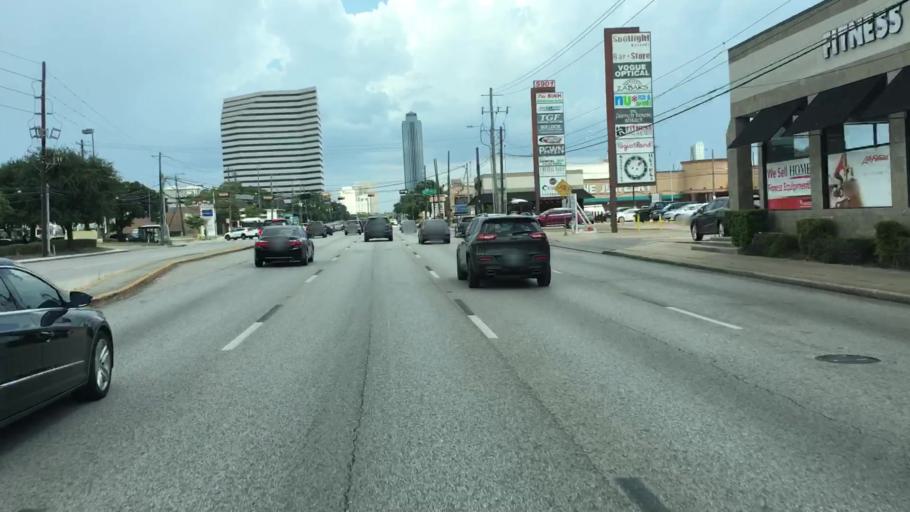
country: US
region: Texas
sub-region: Harris County
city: Hunters Creek Village
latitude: 29.7378
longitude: -95.4856
